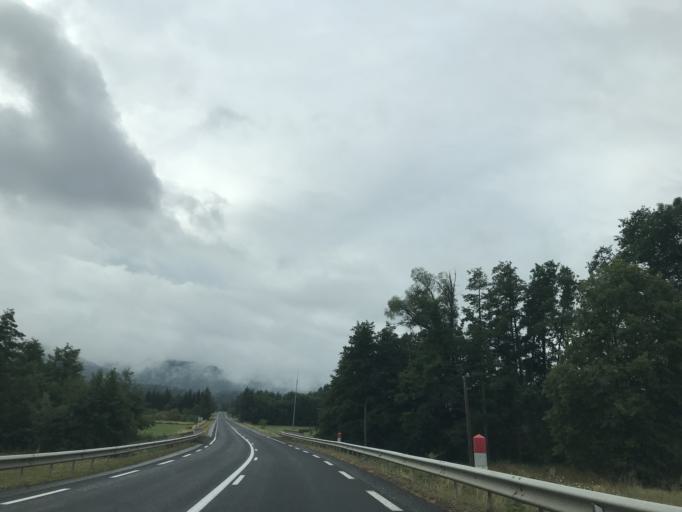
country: FR
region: Auvergne
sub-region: Departement du Puy-de-Dome
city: Arlanc
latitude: 45.3828
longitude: 3.7449
